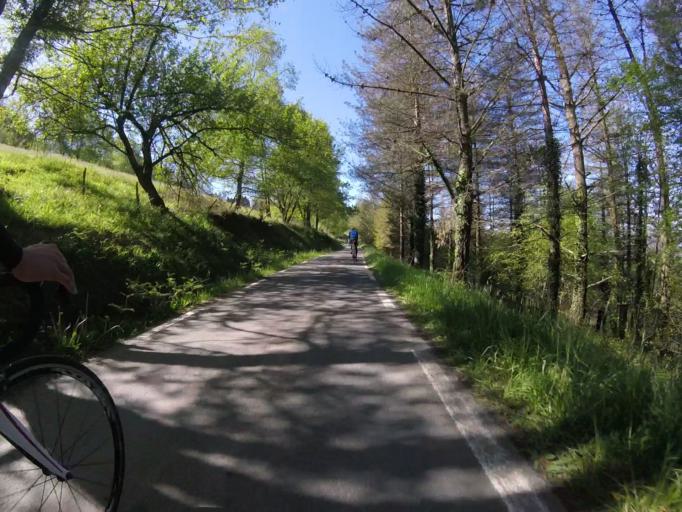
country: ES
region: Basque Country
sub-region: Provincia de Guipuzcoa
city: Errezil
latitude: 43.1948
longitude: -2.2009
